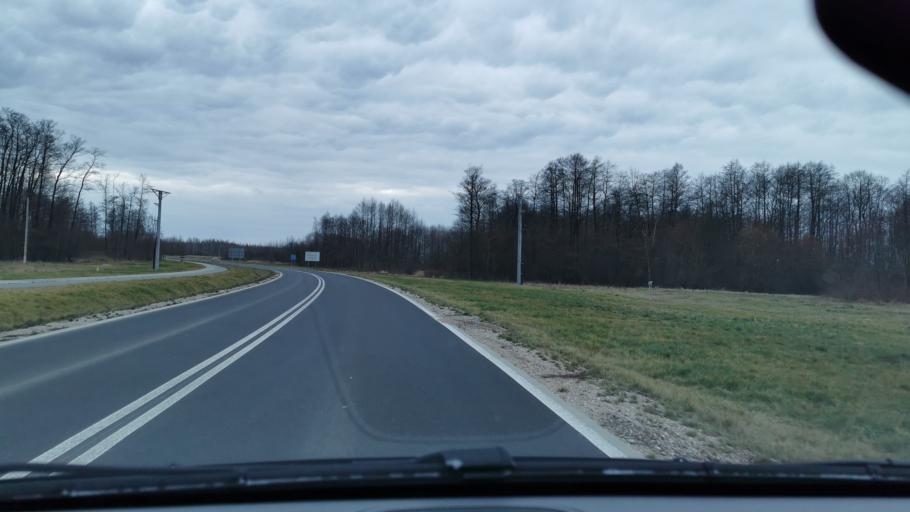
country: PL
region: Masovian Voivodeship
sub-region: Powiat zyrardowski
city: Zyrardow
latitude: 52.0080
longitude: 20.4658
